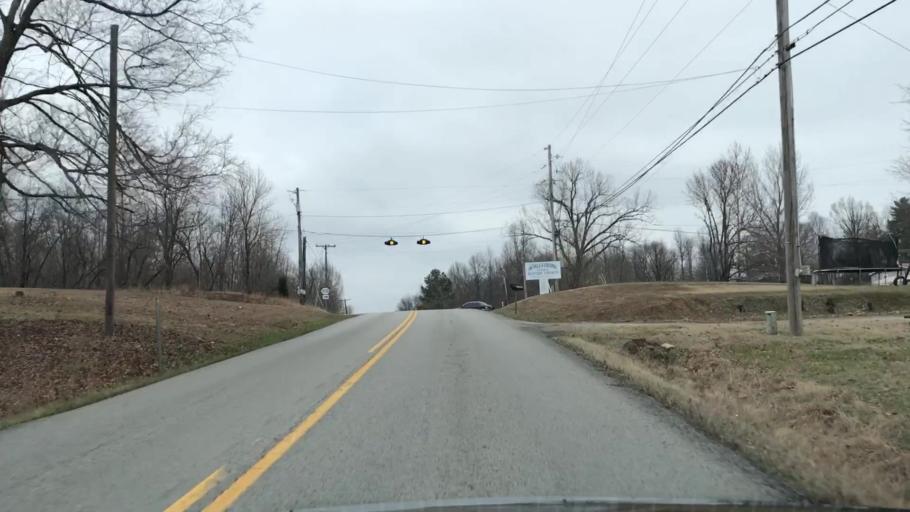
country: US
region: Kentucky
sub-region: Muhlenberg County
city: Morehead
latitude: 37.2416
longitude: -87.1940
